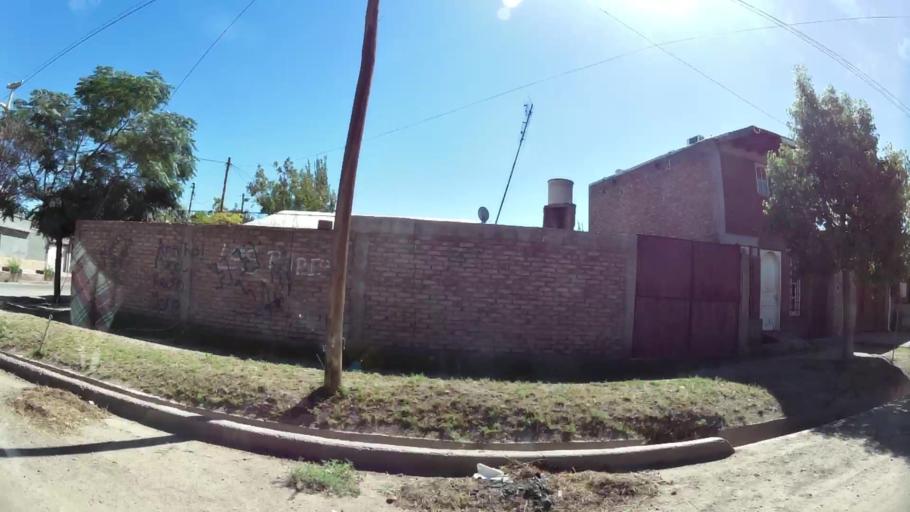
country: AR
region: Mendoza
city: Las Heras
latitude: -32.8284
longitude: -68.8224
